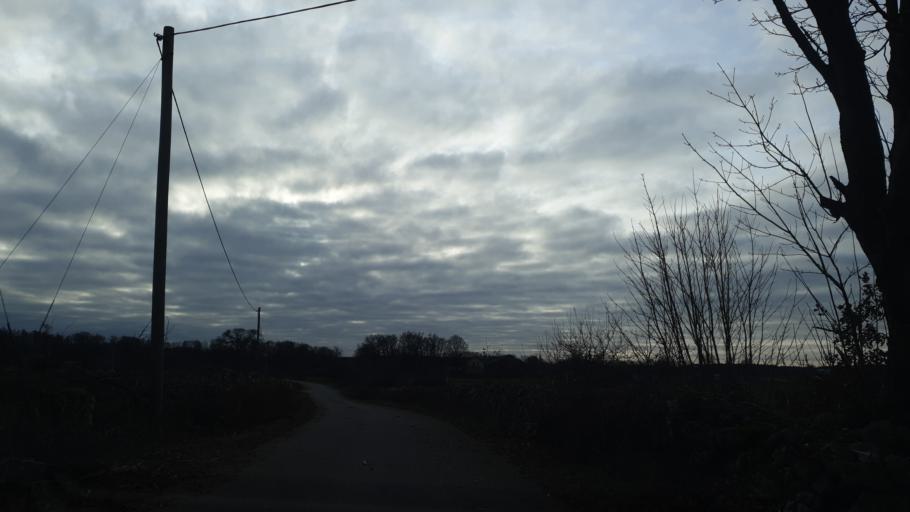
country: SE
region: Kalmar
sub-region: Torsas Kommun
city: Torsas
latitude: 56.3267
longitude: 16.0412
